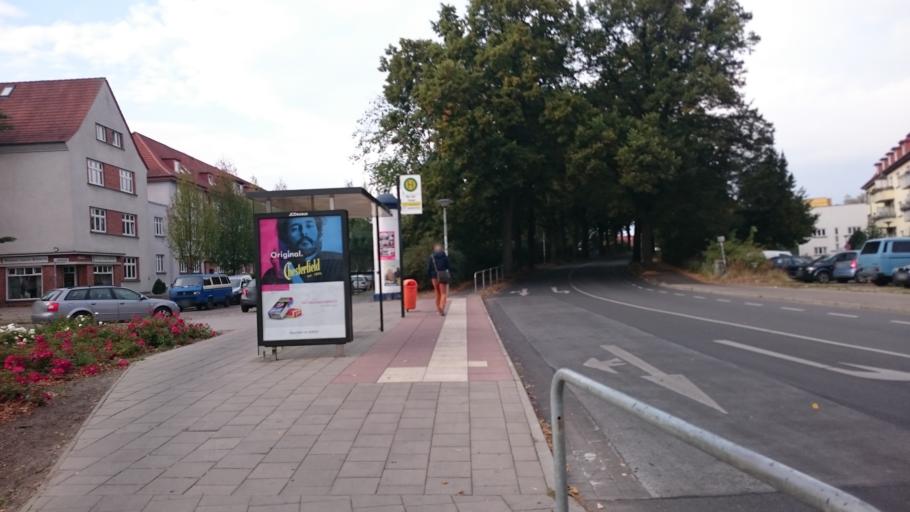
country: DE
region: Mecklenburg-Vorpommern
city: Rostock
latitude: 54.0806
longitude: 12.1136
